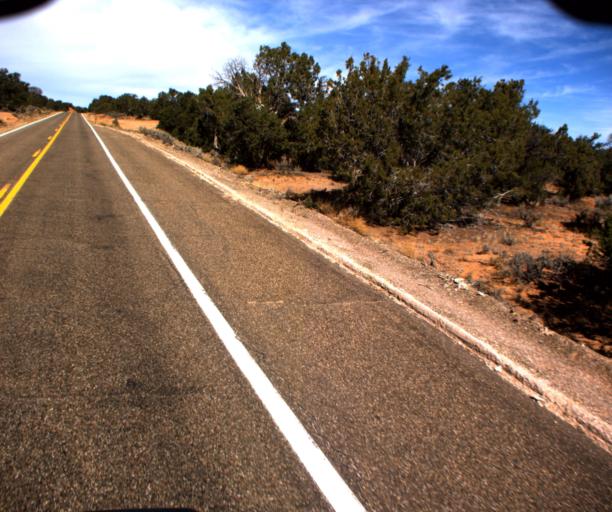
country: US
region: Arizona
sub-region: Navajo County
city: Kayenta
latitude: 36.6170
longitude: -110.5042
